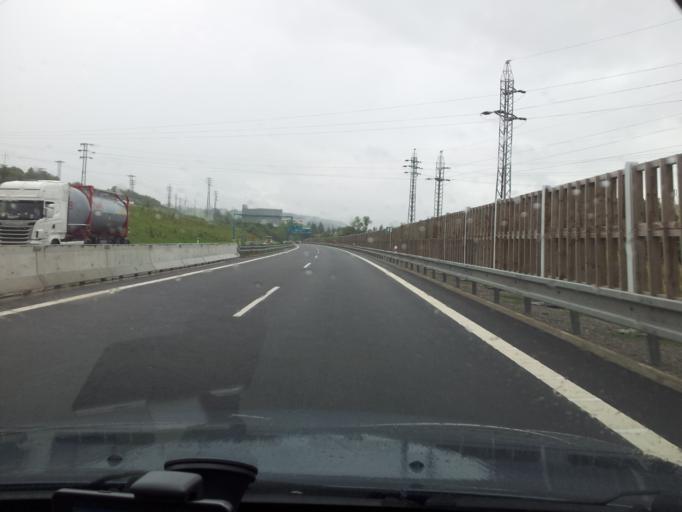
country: SK
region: Banskobystricky
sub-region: Okres Banska Bystrica
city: Banska Bystrica
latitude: 48.7427
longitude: 19.1713
